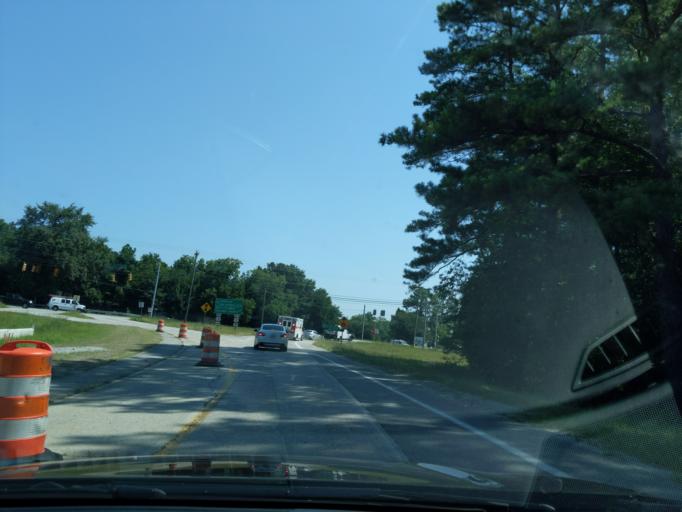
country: US
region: South Carolina
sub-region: Lexington County
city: Lexington
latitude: 33.9772
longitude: -81.1933
